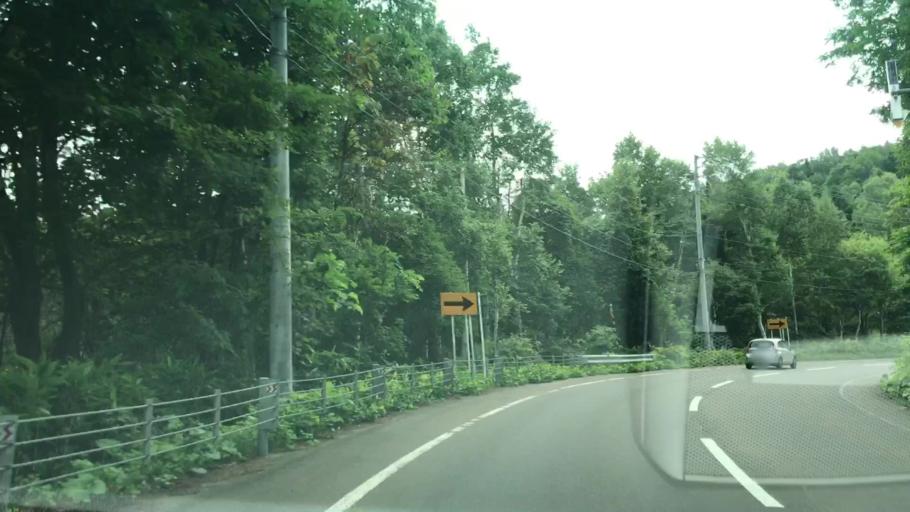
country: JP
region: Hokkaido
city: Yoichi
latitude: 43.1316
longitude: 140.8265
